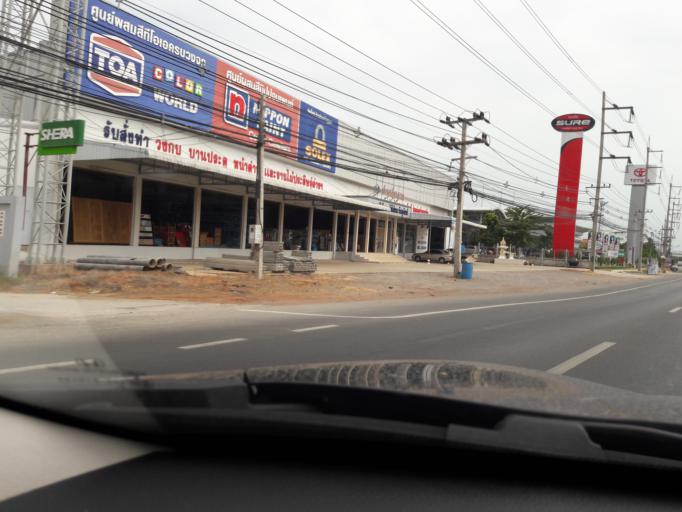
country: TH
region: Ratchaburi
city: Damnoen Saduak
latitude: 13.5474
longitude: 99.9664
